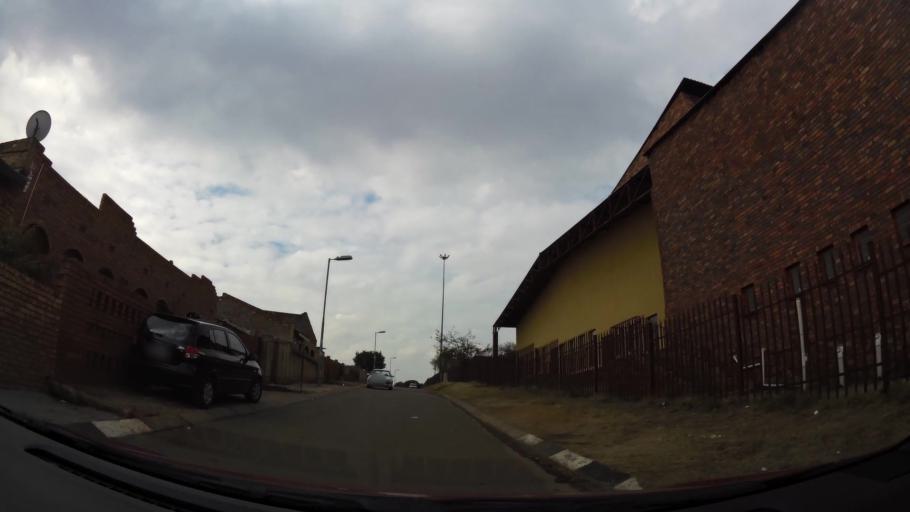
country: ZA
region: Gauteng
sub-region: City of Johannesburg Metropolitan Municipality
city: Soweto
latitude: -26.2537
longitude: 27.8238
